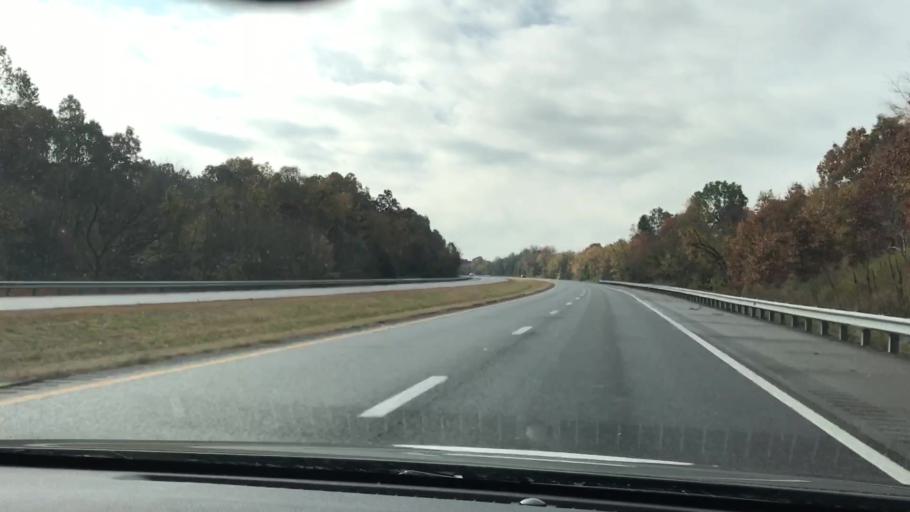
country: US
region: Kentucky
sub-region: Marshall County
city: Calvert City
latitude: 36.9540
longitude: -88.3500
